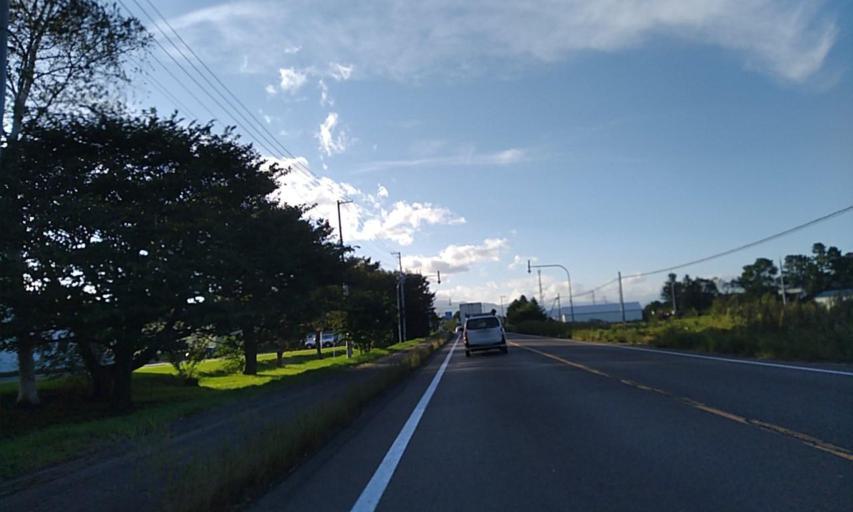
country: JP
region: Hokkaido
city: Otofuke
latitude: 42.9453
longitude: 142.9443
